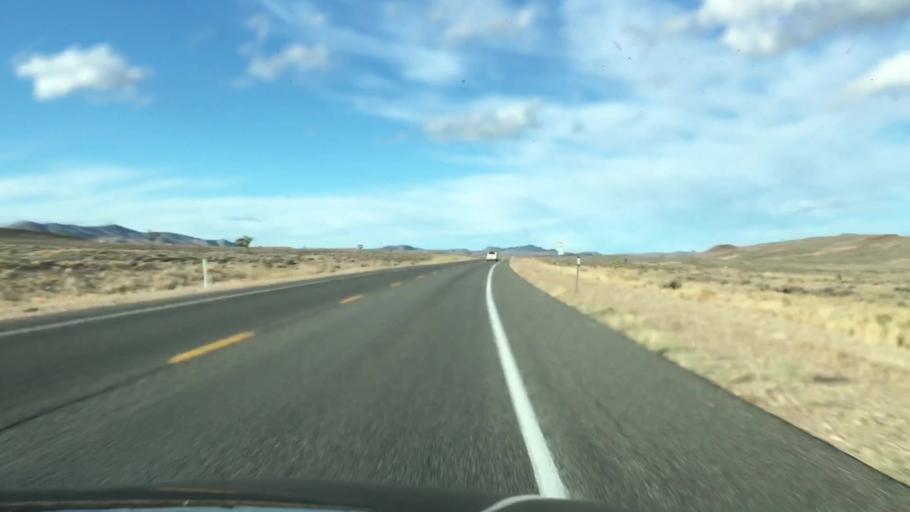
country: US
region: Nevada
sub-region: Esmeralda County
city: Goldfield
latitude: 37.5417
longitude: -117.1953
